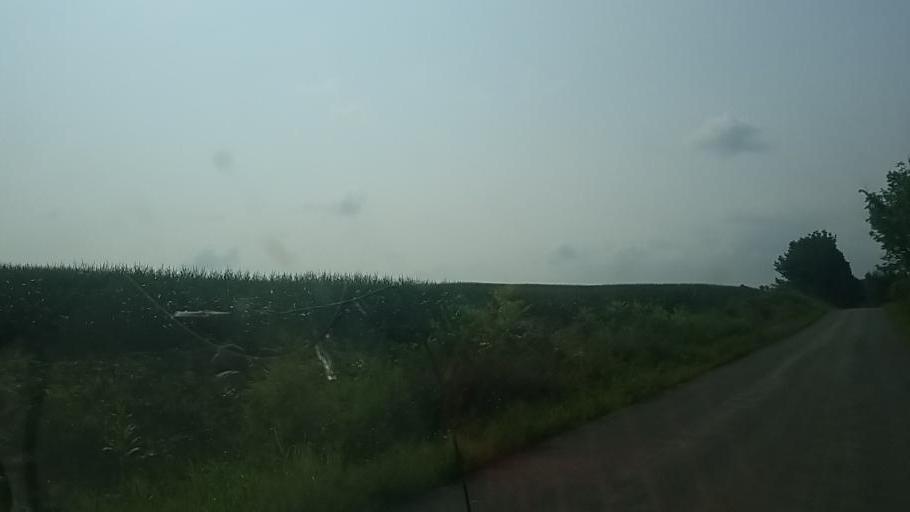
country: US
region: New York
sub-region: Montgomery County
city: Fonda
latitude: 42.9807
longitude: -74.4462
